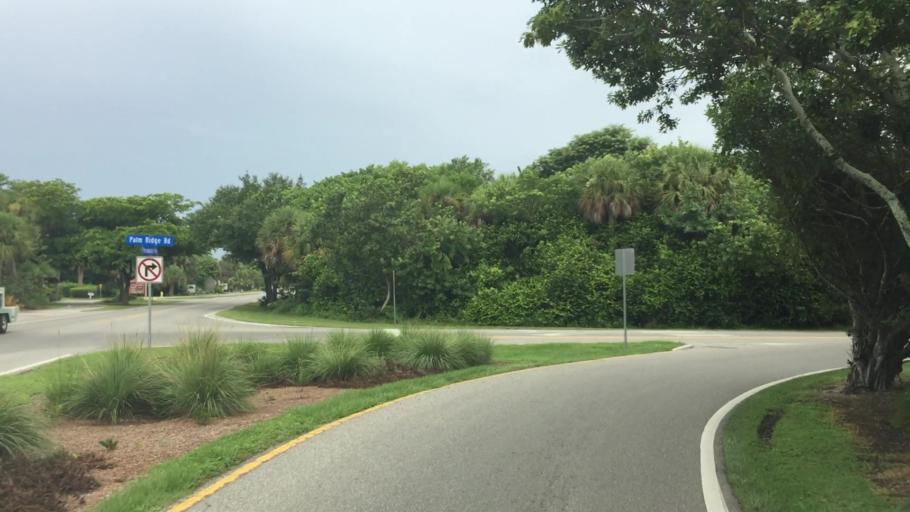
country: US
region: Florida
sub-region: Lee County
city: Sanibel
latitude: 26.4365
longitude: -82.0766
